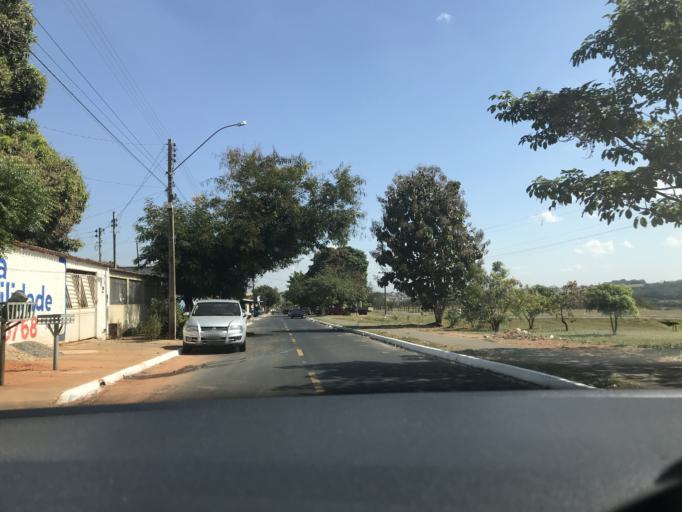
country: BR
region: Goias
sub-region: Senador Canedo
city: Senador Canedo
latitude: -16.6492
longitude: -49.1543
